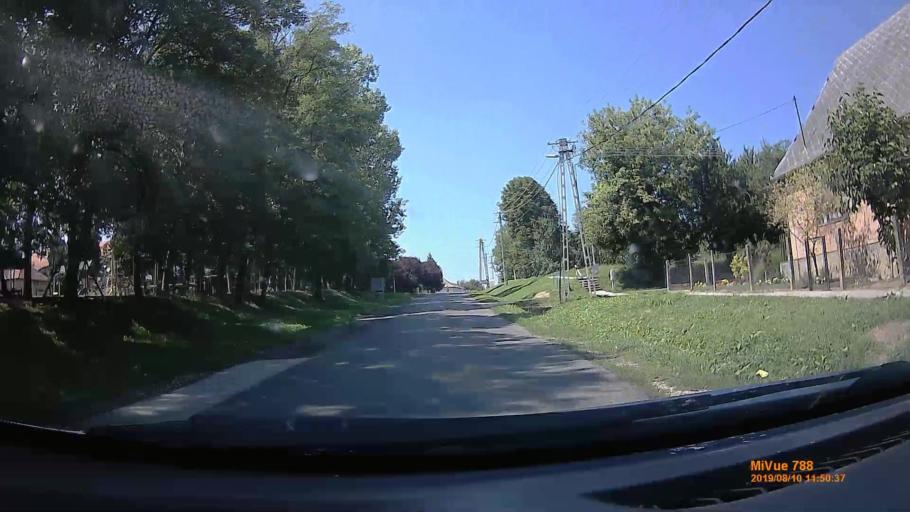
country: HU
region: Somogy
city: Somogyvar
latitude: 46.4918
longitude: 17.7171
